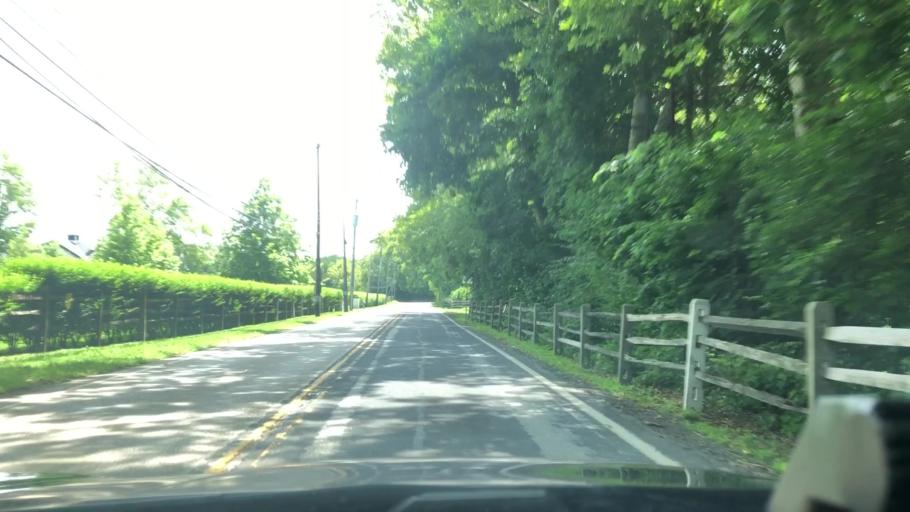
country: US
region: Pennsylvania
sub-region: Montgomery County
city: Flourtown
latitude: 40.0997
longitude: -75.2296
